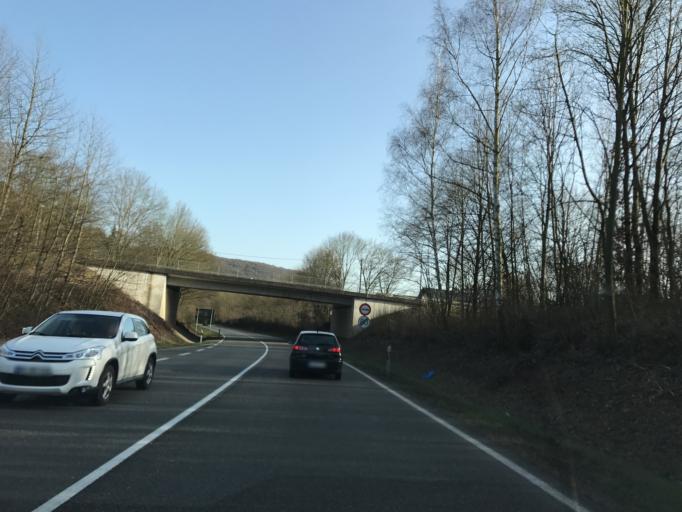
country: DE
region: Rheinland-Pfalz
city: Rheinbrohl
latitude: 50.5079
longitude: 7.3263
